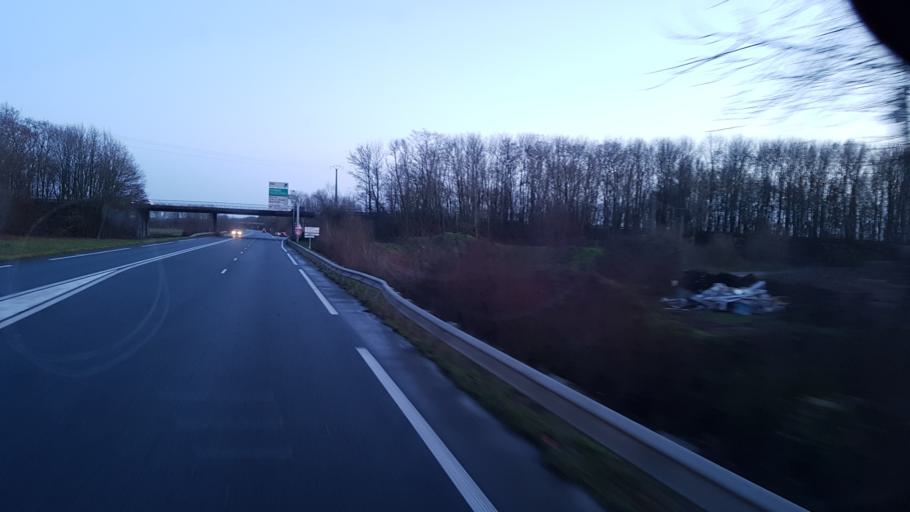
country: FR
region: Nord-Pas-de-Calais
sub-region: Departement du Nord
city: Ferin
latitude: 50.3364
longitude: 3.0882
